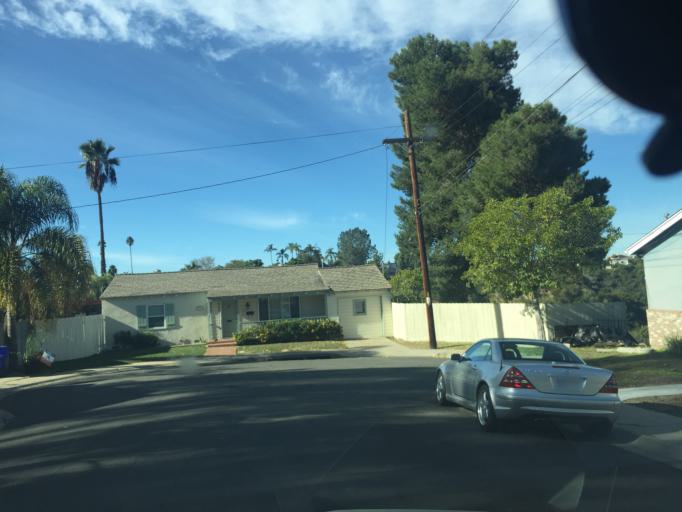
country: US
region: California
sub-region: San Diego County
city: Lemon Grove
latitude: 32.7665
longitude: -117.0827
